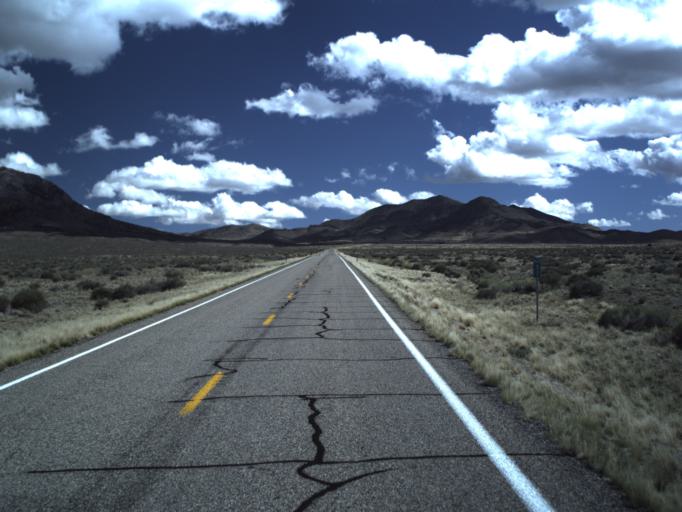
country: US
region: Utah
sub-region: Beaver County
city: Milford
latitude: 38.4489
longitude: -113.3409
